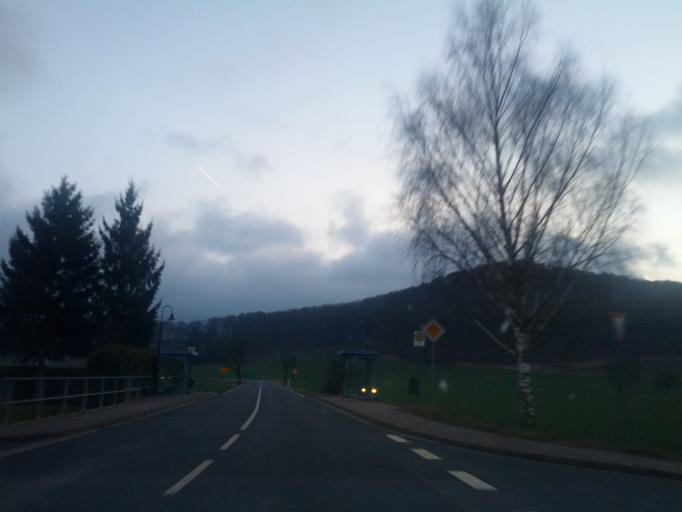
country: DE
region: Thuringia
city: Ifta
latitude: 51.0704
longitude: 10.2064
